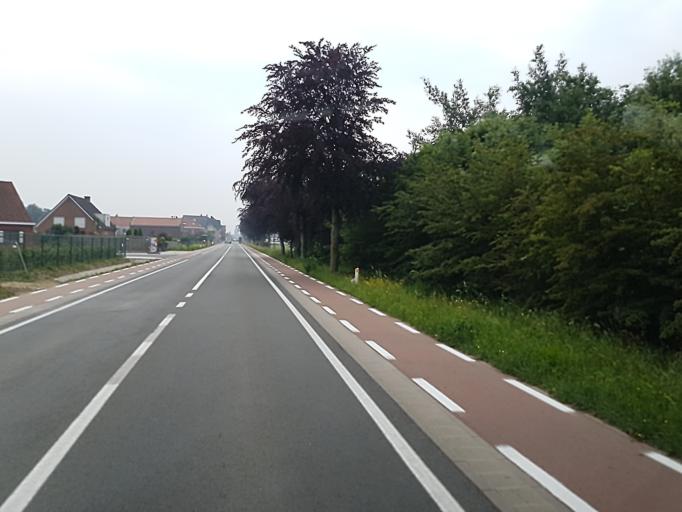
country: BE
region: Flanders
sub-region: Provincie West-Vlaanderen
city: Dentergem
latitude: 50.9410
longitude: 3.3936
